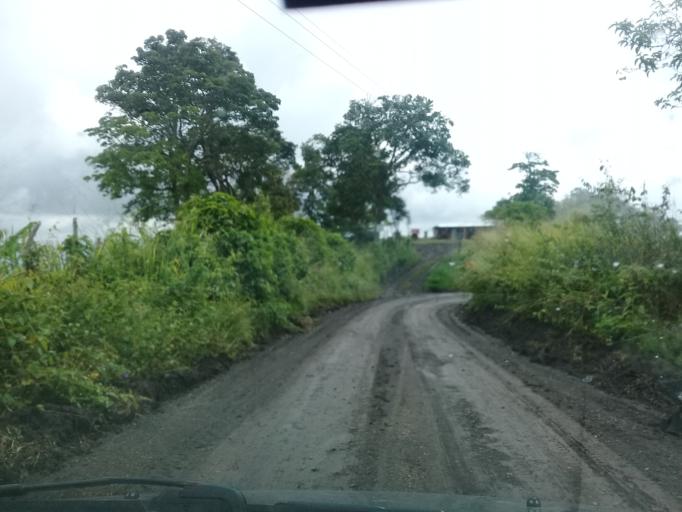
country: CO
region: Cundinamarca
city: Quipile
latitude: 4.7082
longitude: -74.5309
